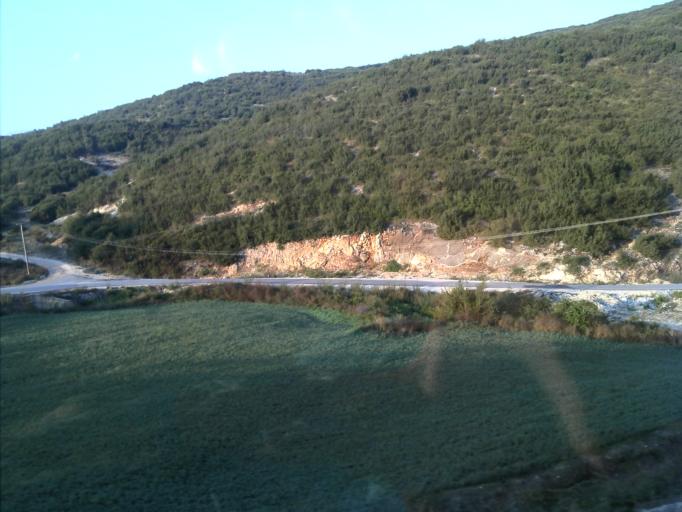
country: AL
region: Fier
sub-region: Rrethi i Mallakastres
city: Fratar
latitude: 40.5104
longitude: 19.8066
